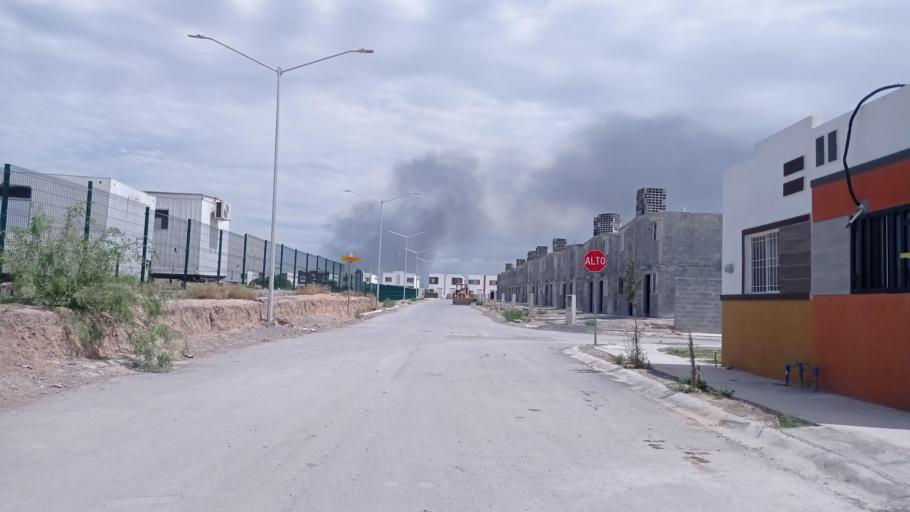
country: MX
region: Nuevo Leon
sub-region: Salinas Victoria
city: Simeprodeso (Colectivo Nuevo)
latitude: 25.8753
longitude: -100.3194
